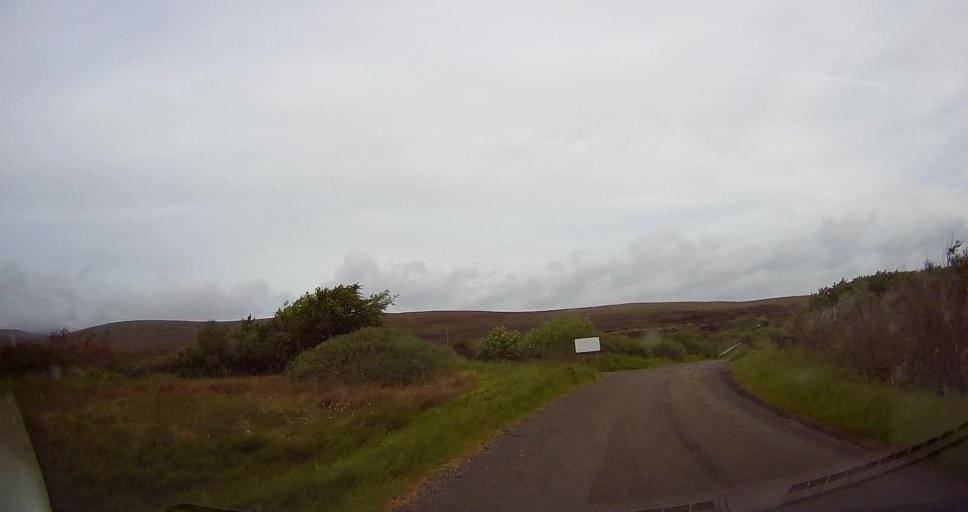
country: GB
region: Scotland
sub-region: Orkney Islands
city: Stromness
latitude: 58.8391
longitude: -3.2169
